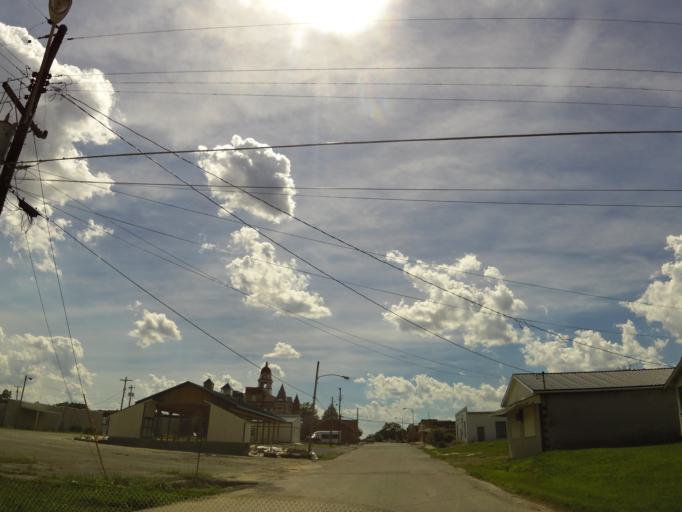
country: US
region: Tennessee
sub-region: Gibson County
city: Trenton
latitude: 35.9818
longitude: -88.9396
